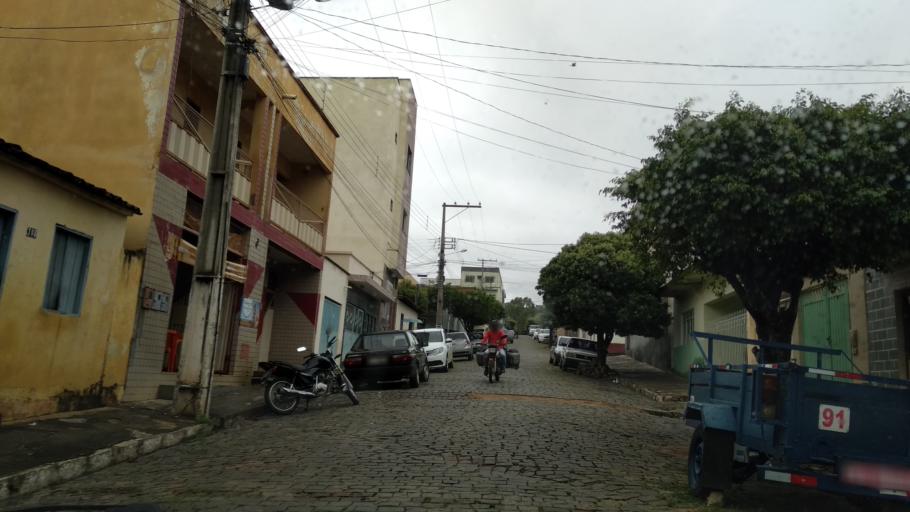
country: BR
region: Bahia
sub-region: Caetite
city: Caetite
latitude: -14.0654
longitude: -42.4916
